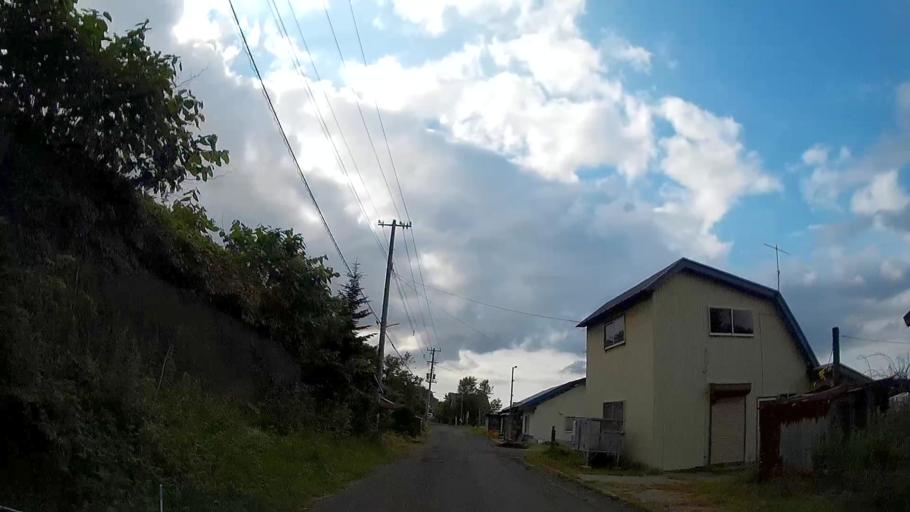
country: JP
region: Hokkaido
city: Nanae
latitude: 42.1145
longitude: 140.5451
